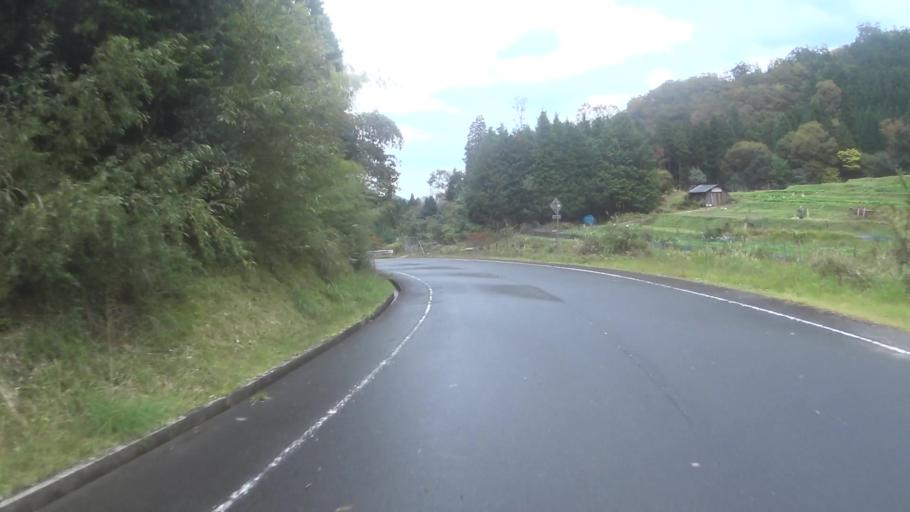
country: JP
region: Kyoto
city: Miyazu
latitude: 35.5006
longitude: 135.0444
